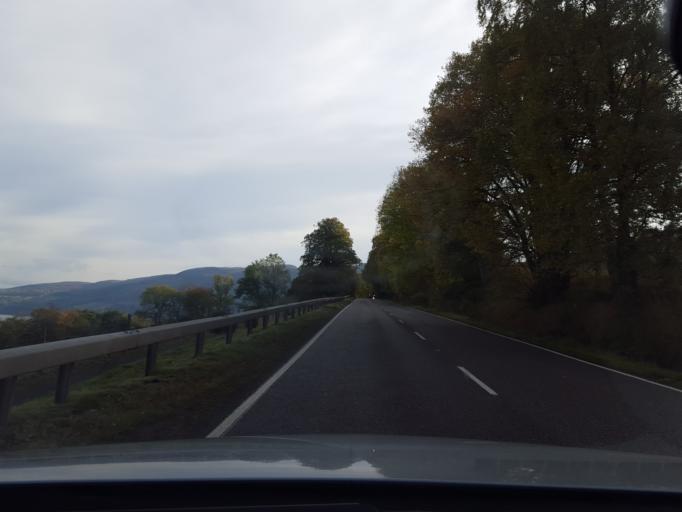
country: GB
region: Scotland
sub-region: Highland
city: Beauly
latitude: 57.3277
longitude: -4.4558
